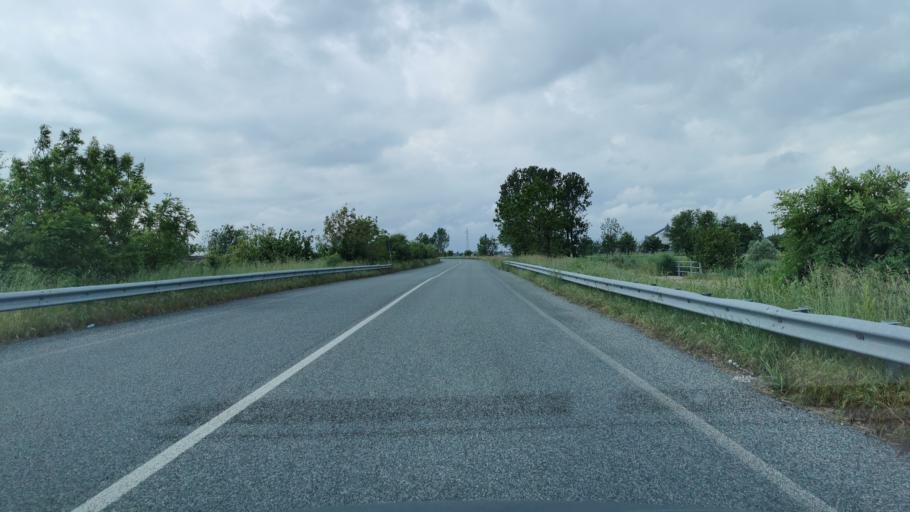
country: IT
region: Piedmont
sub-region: Provincia di Cuneo
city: Racconigi
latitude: 44.7893
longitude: 7.7009
